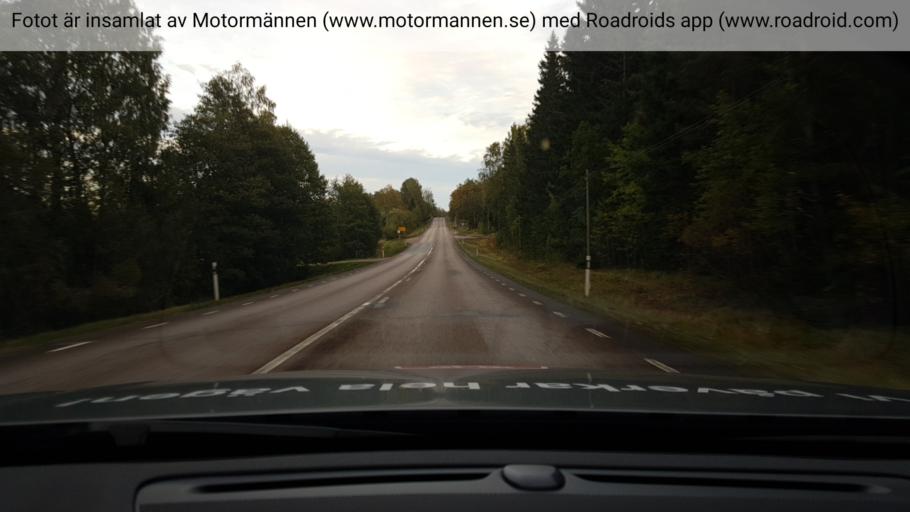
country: SE
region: Vaestra Goetaland
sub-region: Amals Kommun
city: Amal
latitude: 59.0747
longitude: 12.5836
